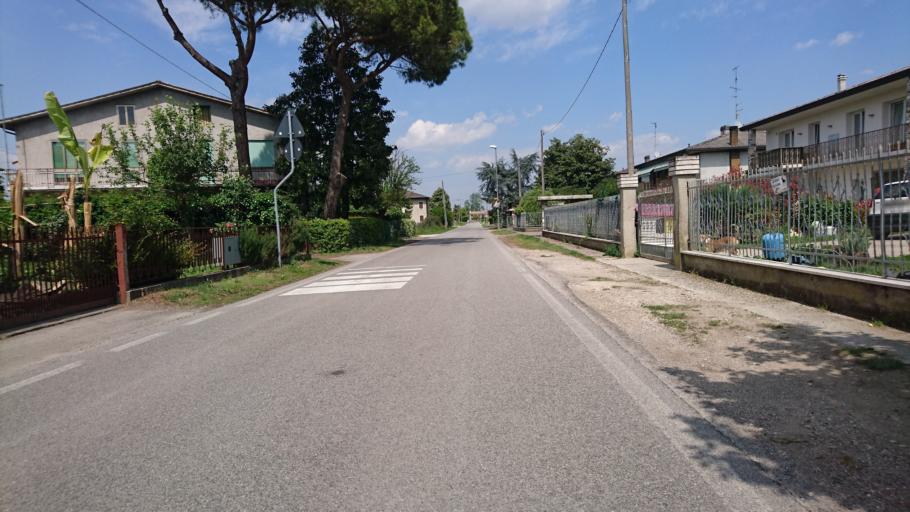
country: IT
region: Veneto
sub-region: Provincia di Padova
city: Saccolongo
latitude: 45.4041
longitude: 11.7314
